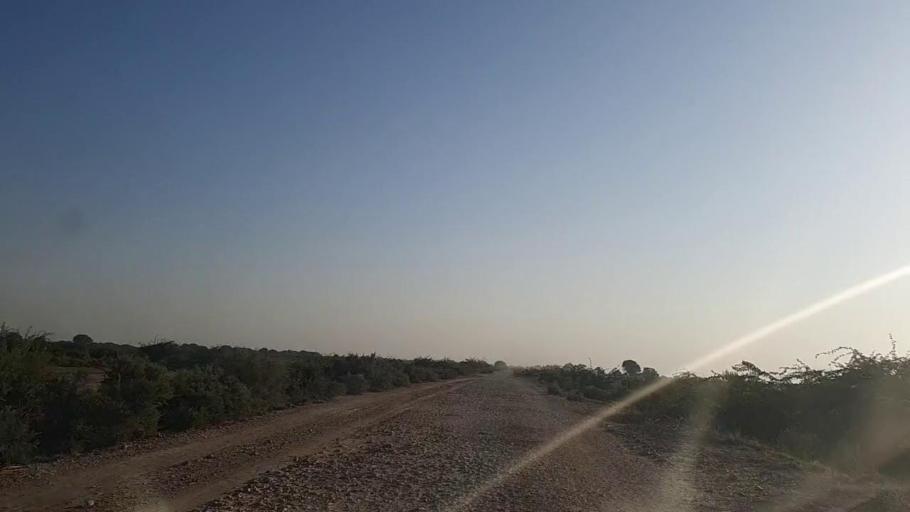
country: PK
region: Sindh
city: Jati
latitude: 24.4373
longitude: 68.1925
